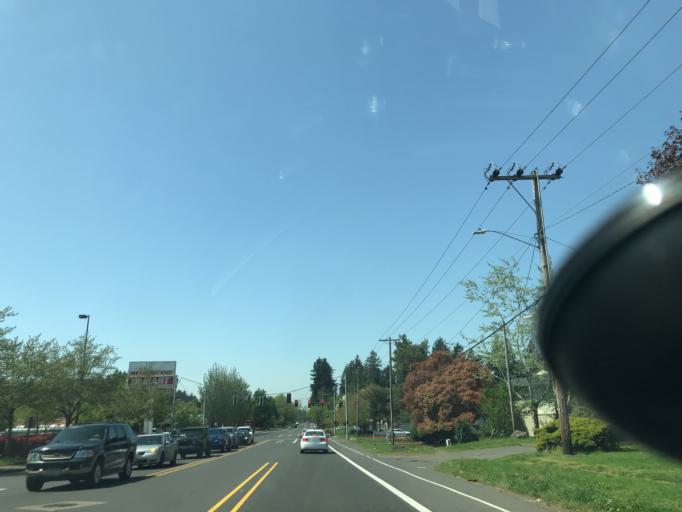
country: US
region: Oregon
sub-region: Multnomah County
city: Gresham
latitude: 45.4925
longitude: -122.4854
